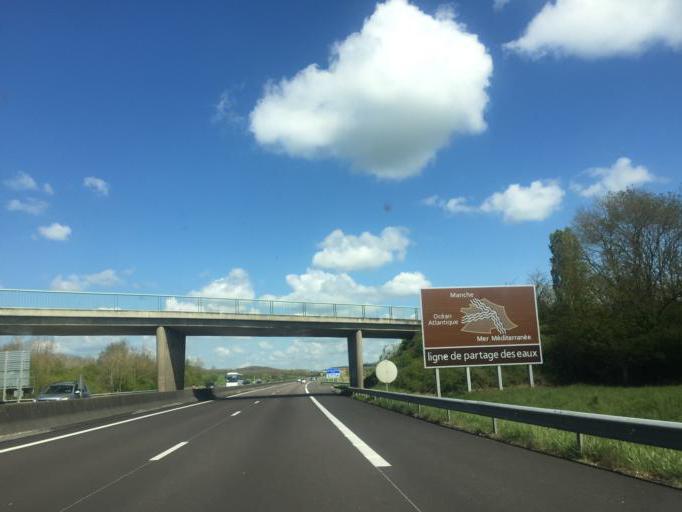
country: FR
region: Bourgogne
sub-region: Departement de la Cote-d'Or
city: Pouilly-en-Auxois
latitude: 47.2250
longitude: 4.5904
